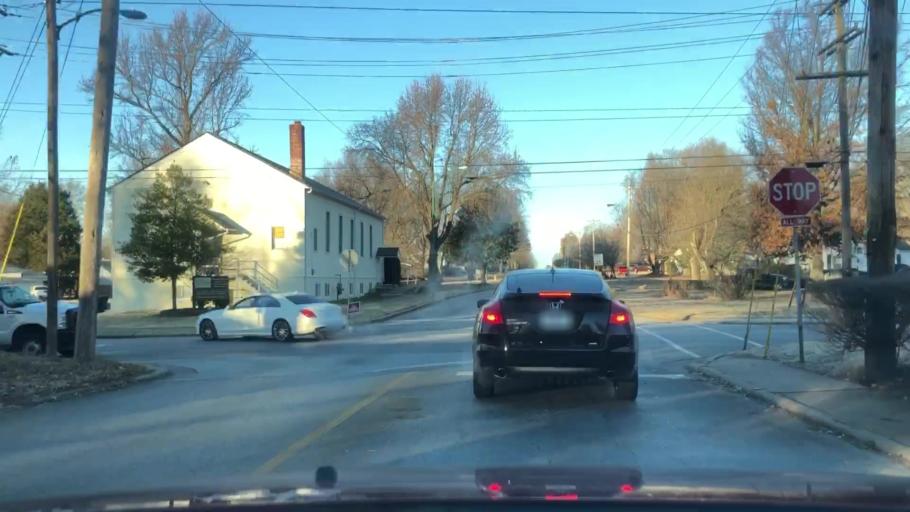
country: US
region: Missouri
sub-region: Greene County
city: Springfield
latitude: 37.1736
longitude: -93.2463
